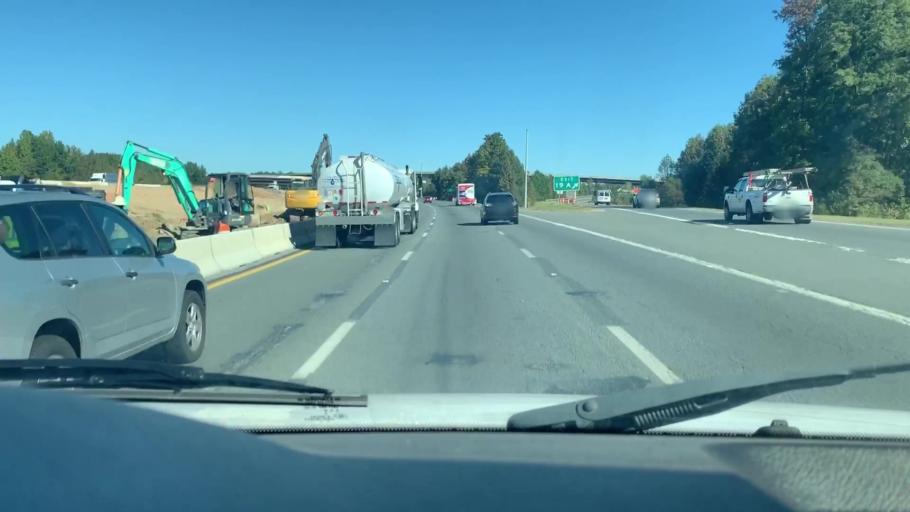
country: US
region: North Carolina
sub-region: Mecklenburg County
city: Huntersville
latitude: 35.3591
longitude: -80.8428
